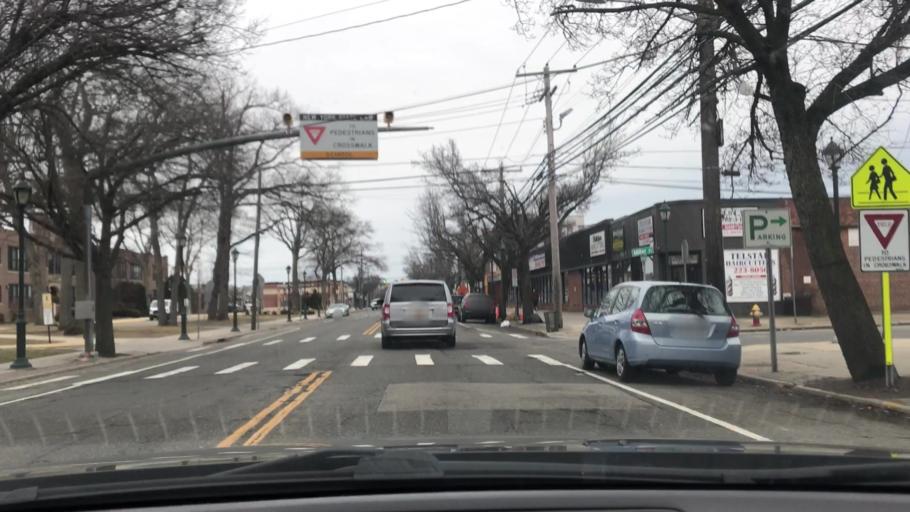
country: US
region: New York
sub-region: Nassau County
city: Merrick
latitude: 40.6679
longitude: -73.5540
